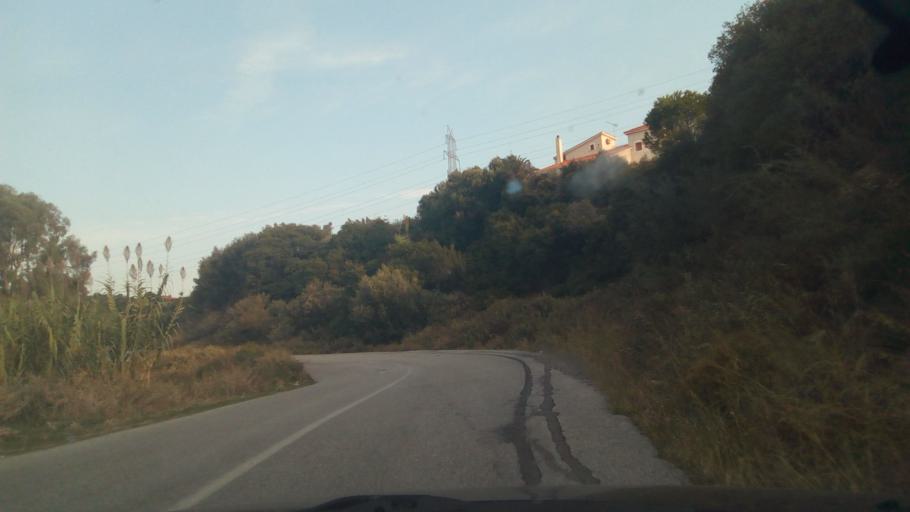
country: GR
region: West Greece
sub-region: Nomos Aitolias kai Akarnanias
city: Nafpaktos
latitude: 38.4105
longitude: 21.9289
